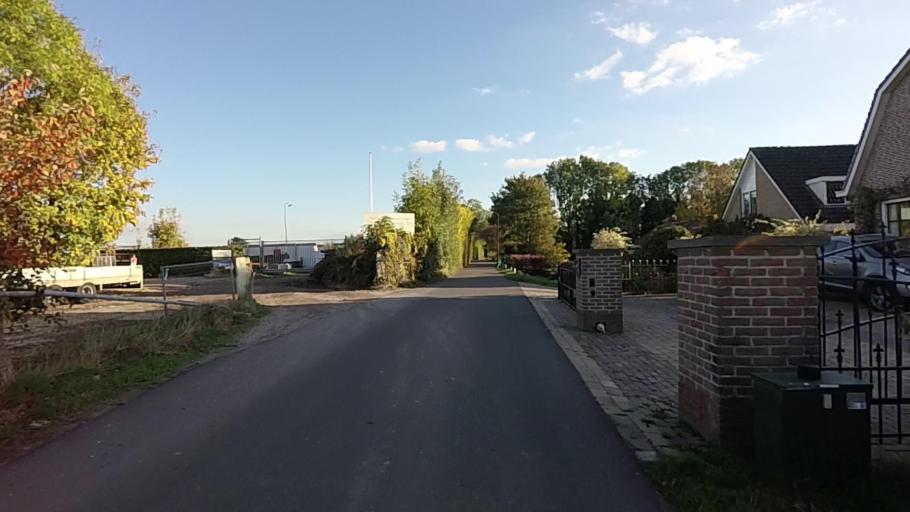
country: NL
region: North Holland
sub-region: Gemeente Amsterdam
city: Driemond
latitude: 52.2696
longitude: 5.0239
